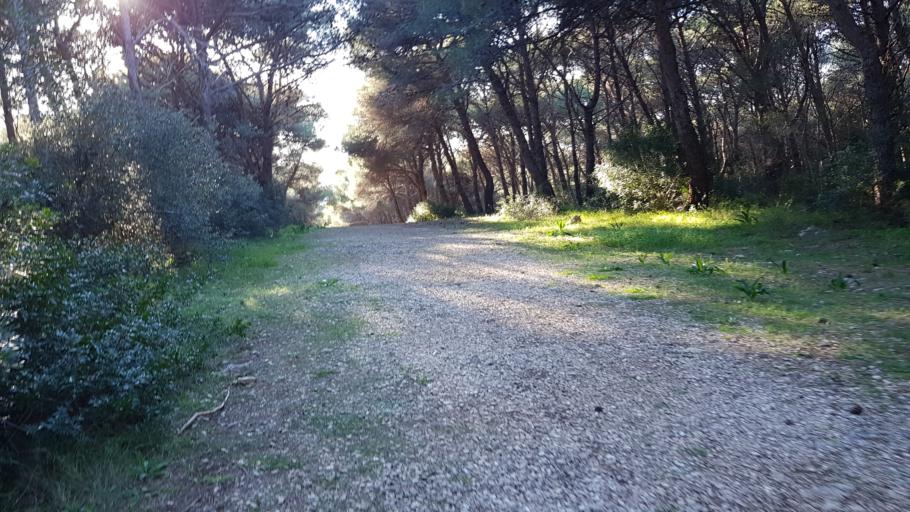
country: IT
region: Apulia
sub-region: Provincia di Lecce
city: Nardo
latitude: 40.1536
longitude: 17.9726
